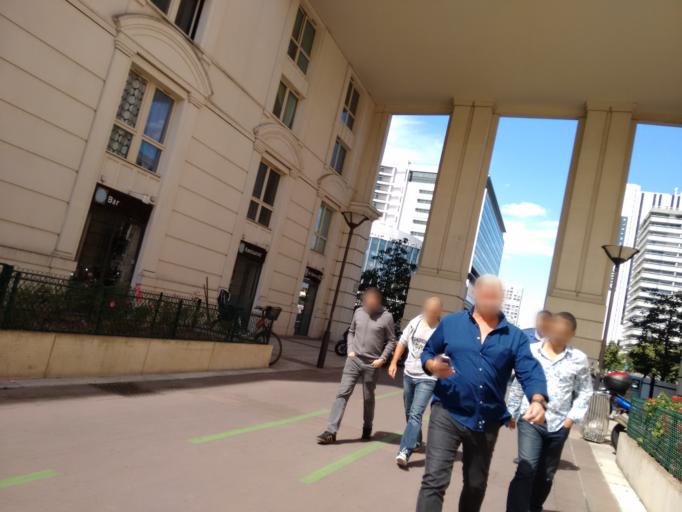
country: FR
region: Ile-de-France
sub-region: Departement des Hauts-de-Seine
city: Montrouge
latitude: 48.8367
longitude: 2.3178
